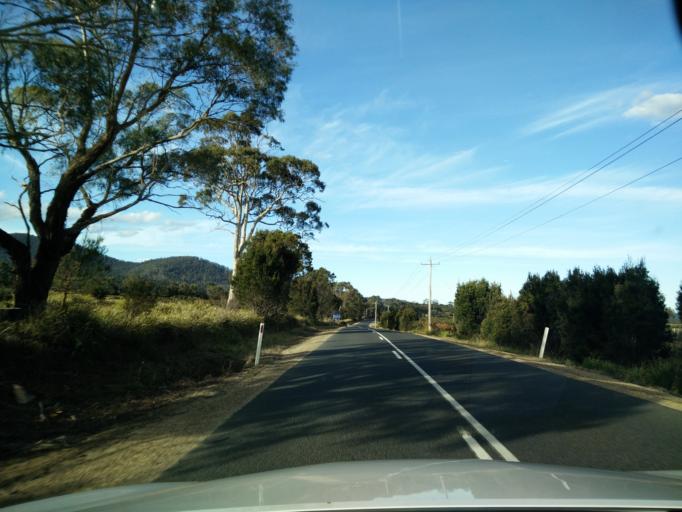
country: AU
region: Tasmania
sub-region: Break O'Day
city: St Helens
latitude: -41.9322
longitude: 148.2265
